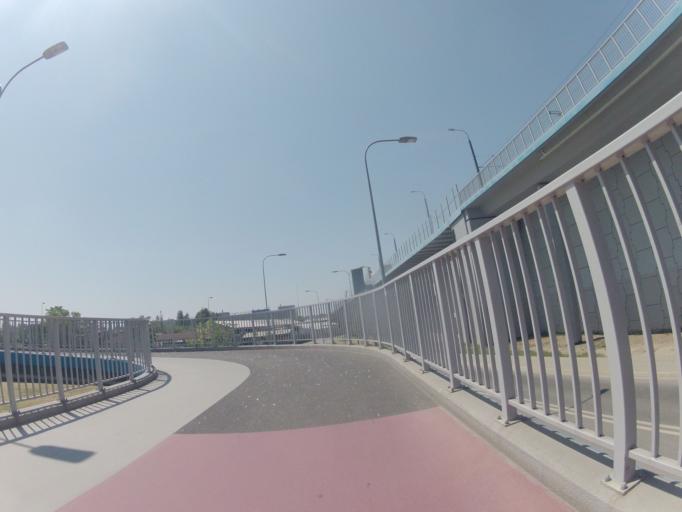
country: PL
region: Lesser Poland Voivodeship
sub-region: Krakow
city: Krakow
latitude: 50.0357
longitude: 19.9812
